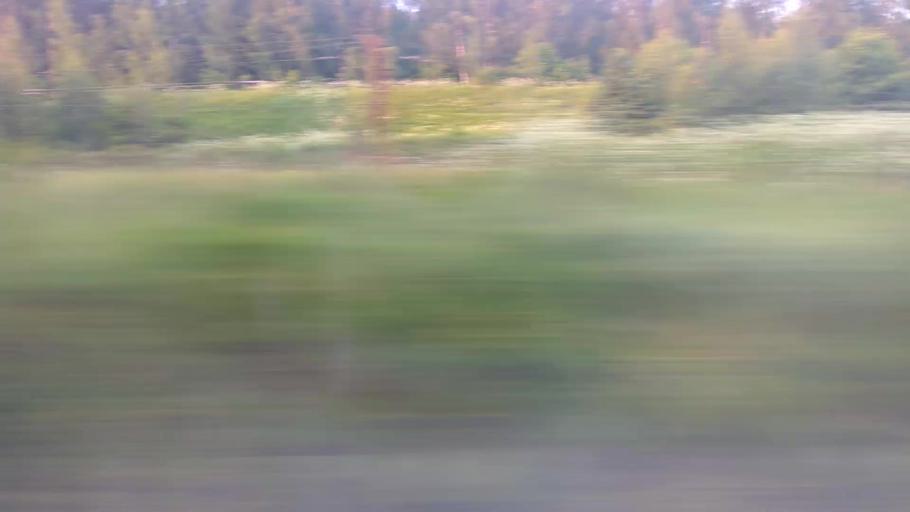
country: RU
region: Moskovskaya
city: Il'inskoye
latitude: 55.1984
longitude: 37.9240
